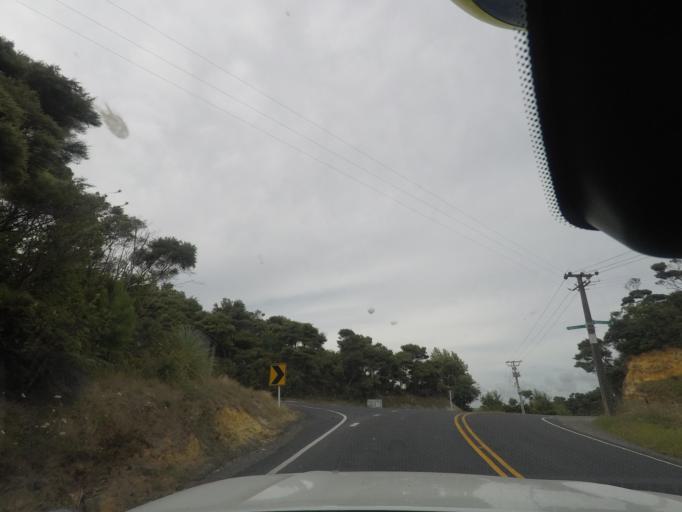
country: NZ
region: Auckland
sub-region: Auckland
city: Parakai
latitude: -36.5778
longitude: 174.3261
